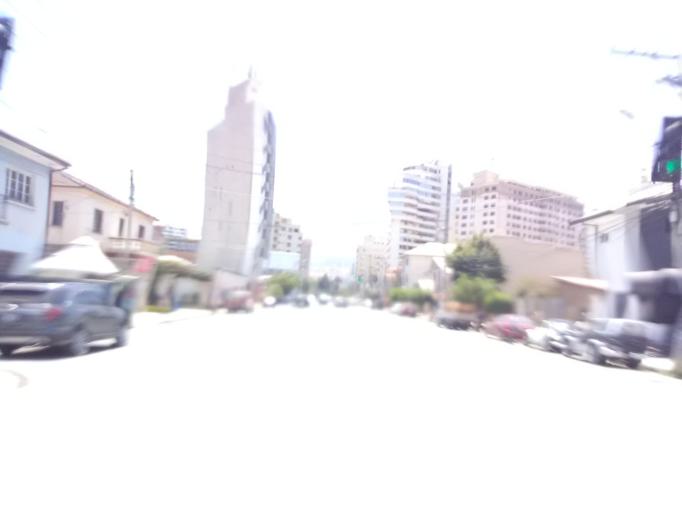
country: BO
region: Cochabamba
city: Cochabamba
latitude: -17.3866
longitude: -66.1509
